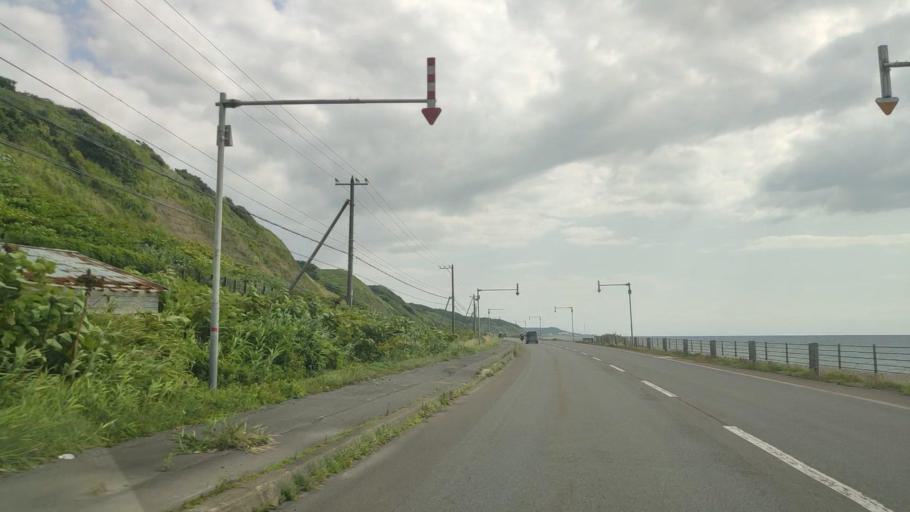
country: JP
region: Hokkaido
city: Rumoi
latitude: 44.1969
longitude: 141.6578
